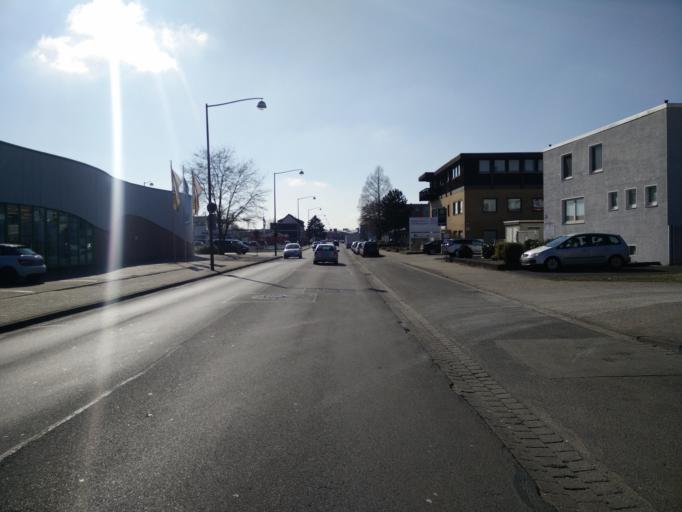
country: DE
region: Lower Saxony
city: Langenhagen
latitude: 52.4331
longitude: 9.7212
